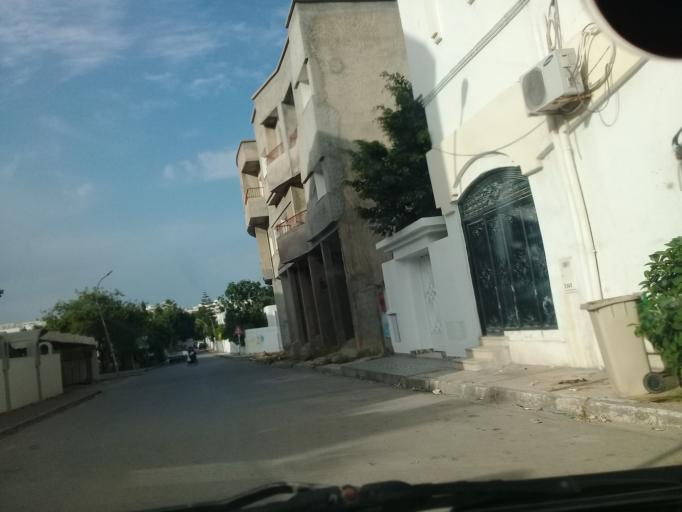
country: TN
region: Ariana
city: Ariana
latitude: 36.8624
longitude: 10.1693
